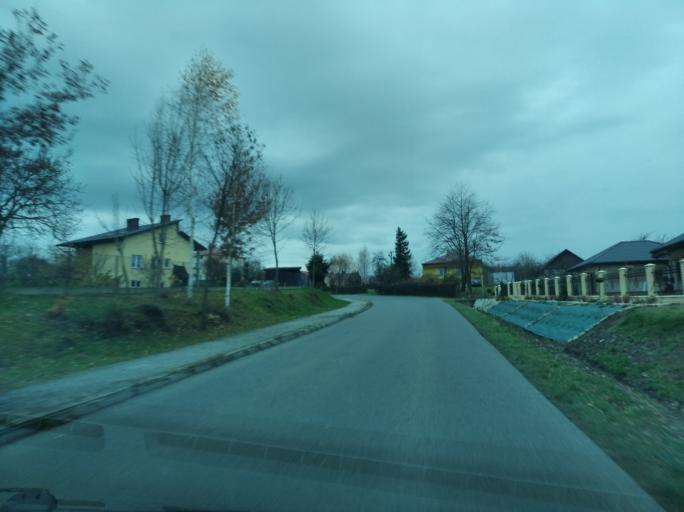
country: PL
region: Subcarpathian Voivodeship
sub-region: Powiat ropczycko-sedziszowski
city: Iwierzyce
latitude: 49.9913
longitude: 21.7298
